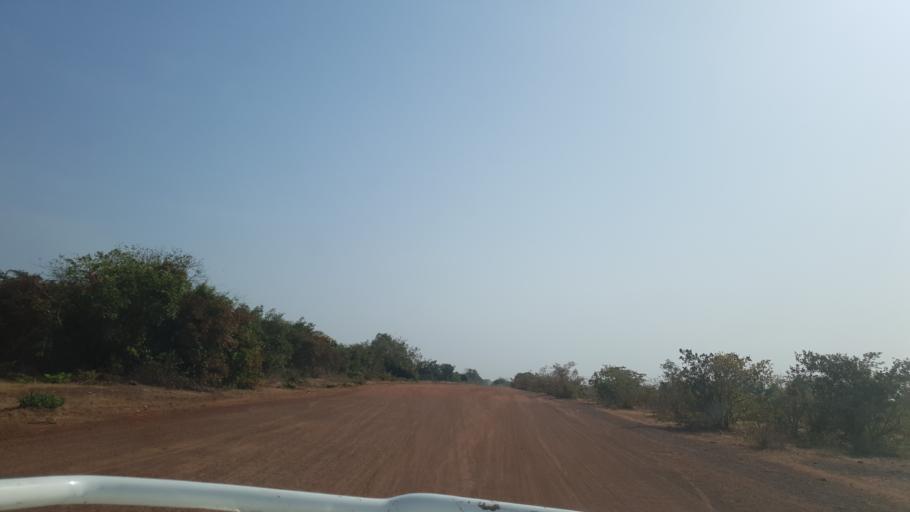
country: ML
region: Koulikoro
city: Dioila
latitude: 12.6677
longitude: -6.6945
